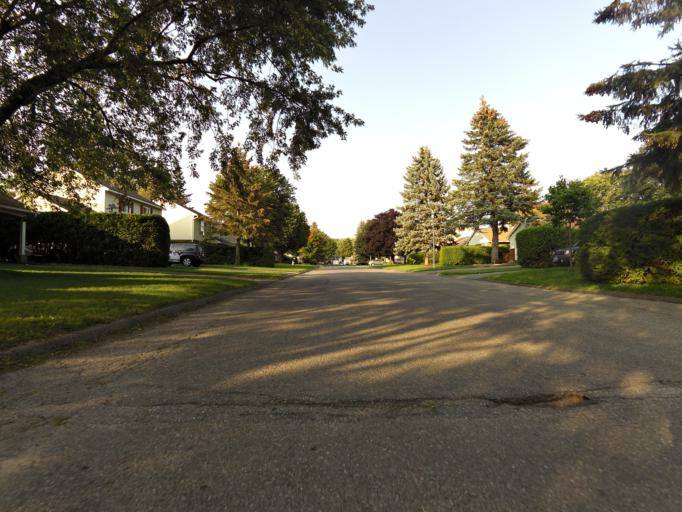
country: CA
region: Ontario
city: Bells Corners
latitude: 45.2959
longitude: -75.8831
